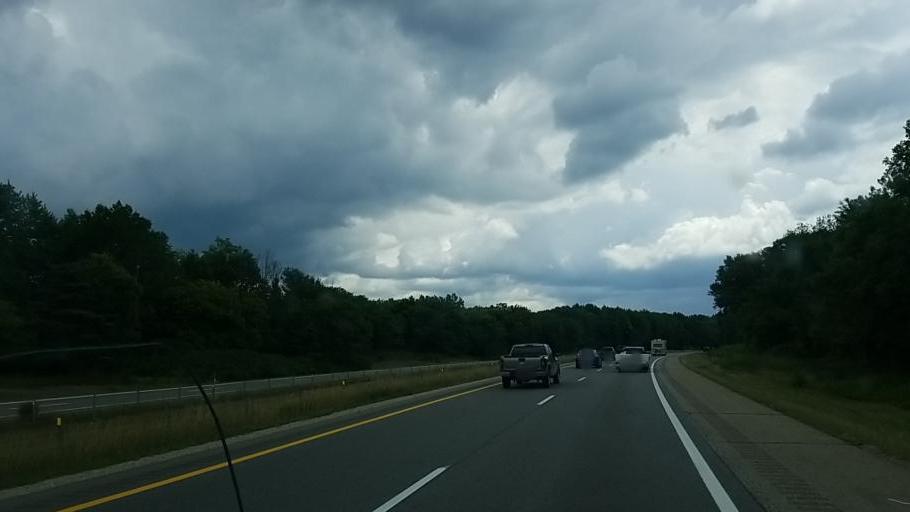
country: US
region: Michigan
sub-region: Kent County
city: Northview
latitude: 43.0110
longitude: -85.6080
